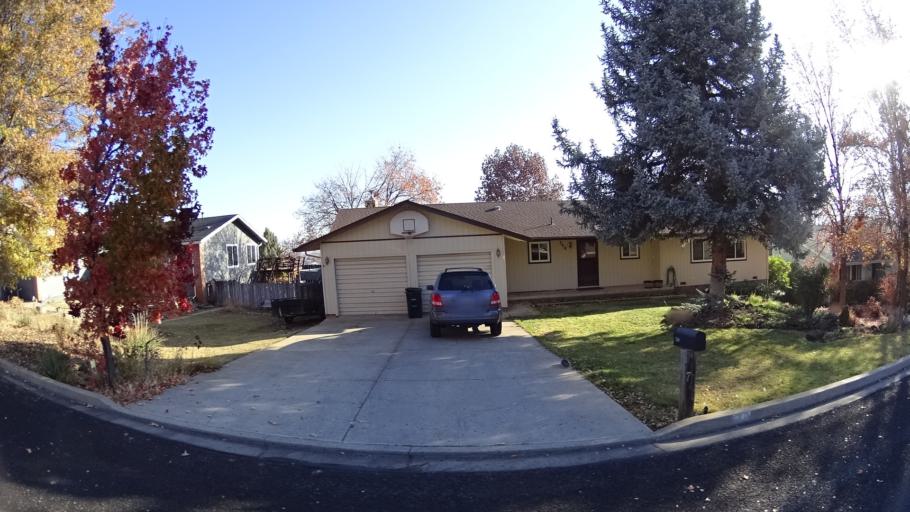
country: US
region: California
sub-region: Siskiyou County
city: Yreka
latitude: 41.7240
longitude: -122.6501
